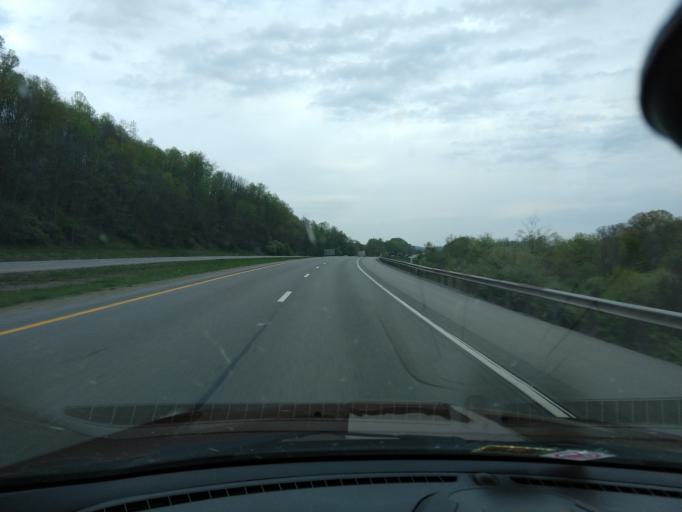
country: US
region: West Virginia
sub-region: Lewis County
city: Weston
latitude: 39.0740
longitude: -80.4049
